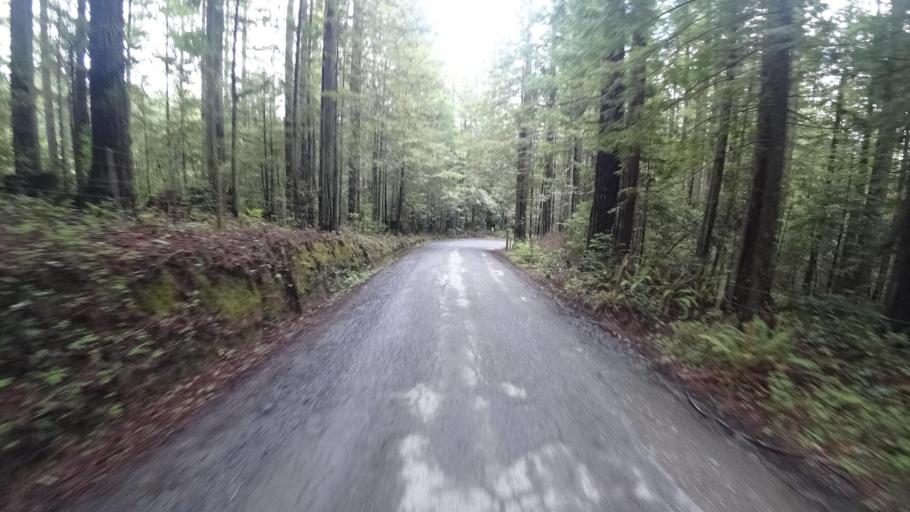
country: US
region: California
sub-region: Humboldt County
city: Blue Lake
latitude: 40.9051
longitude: -123.9753
